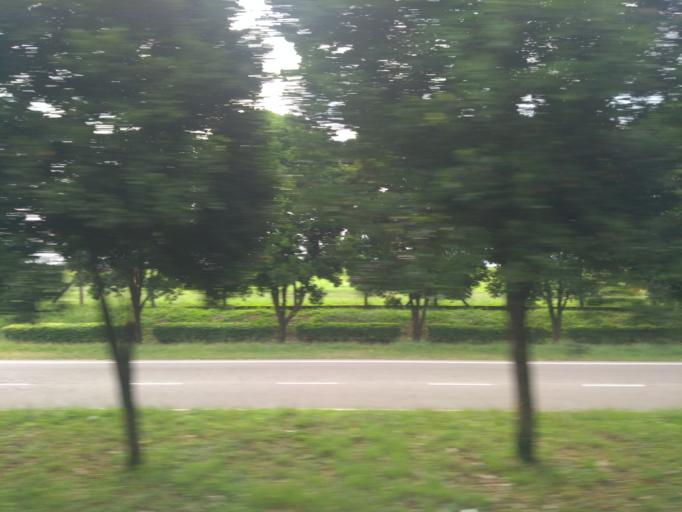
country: MY
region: Melaka
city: Batu Berendam
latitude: 2.2679
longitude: 102.2563
